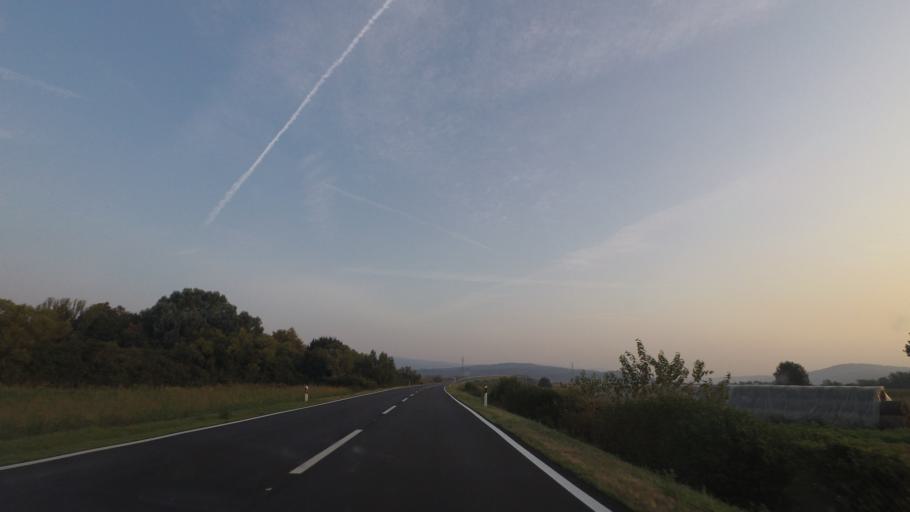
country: HR
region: Brodsko-Posavska
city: Nova Gradiska
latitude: 45.2421
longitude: 17.4089
